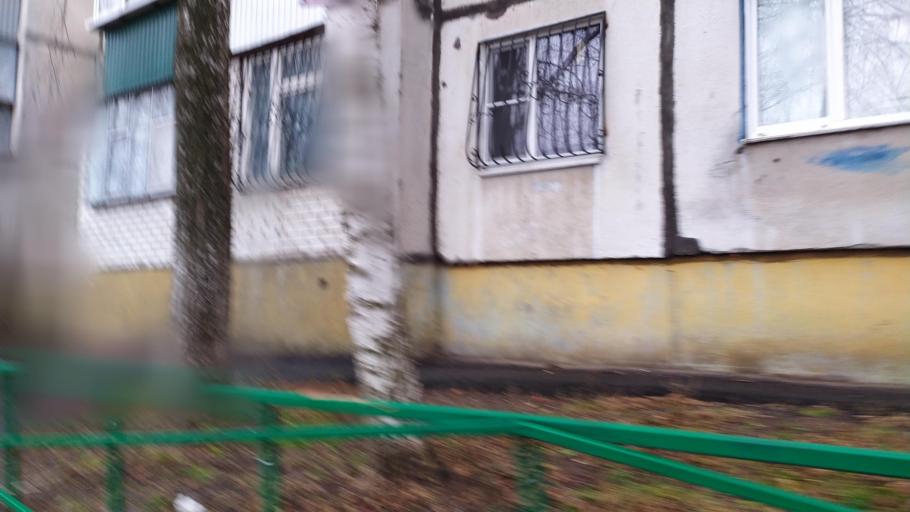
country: RU
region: Kursk
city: Kursk
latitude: 51.7437
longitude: 36.1351
